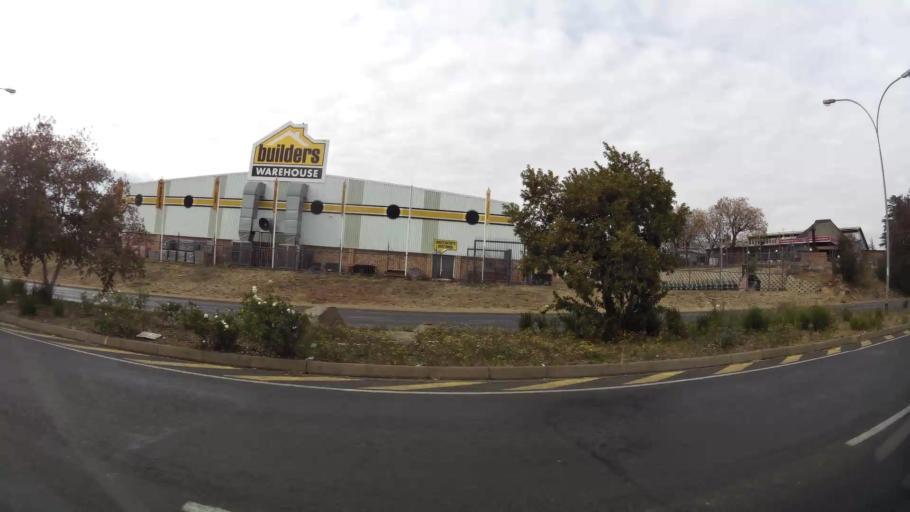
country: ZA
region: Orange Free State
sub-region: Mangaung Metropolitan Municipality
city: Bloemfontein
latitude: -29.1384
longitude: 26.2009
